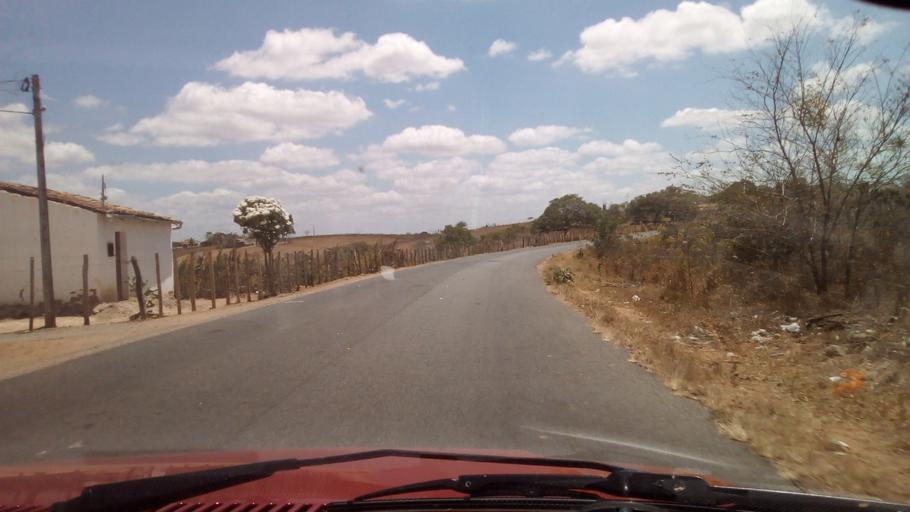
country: BR
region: Paraiba
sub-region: Cacimba De Dentro
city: Cacimba de Dentro
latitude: -6.6183
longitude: -35.8006
